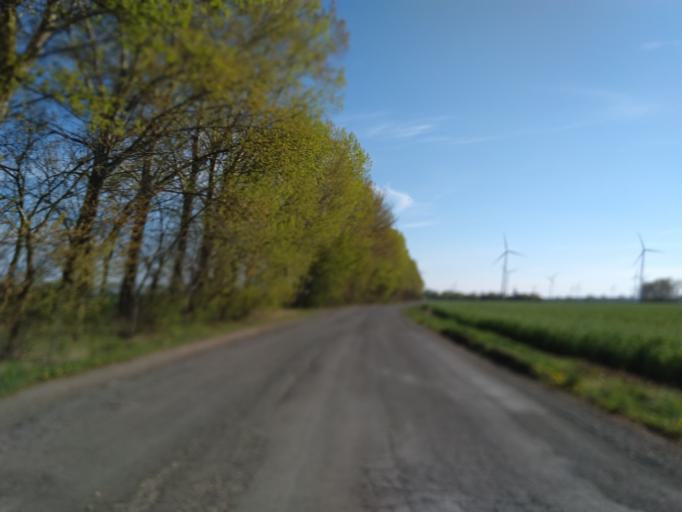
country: DE
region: Brandenburg
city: Neutrebbin
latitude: 52.7244
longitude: 14.2140
